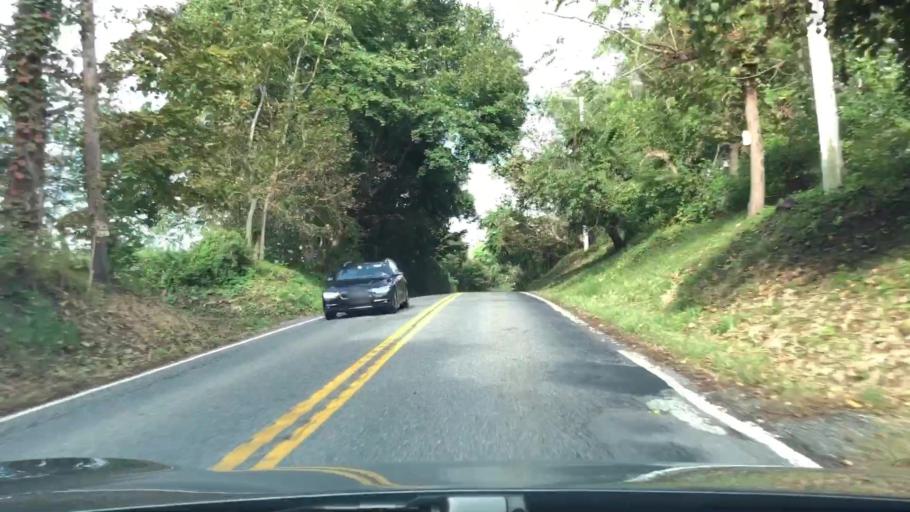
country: US
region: Pennsylvania
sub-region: Delaware County
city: Wayne
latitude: 40.0094
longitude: -75.3803
